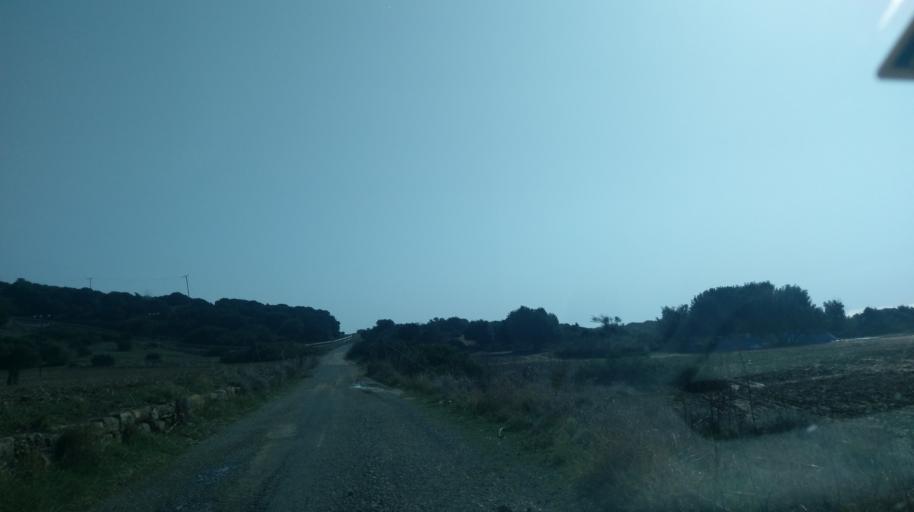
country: CY
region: Ammochostos
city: Rizokarpaso
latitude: 35.6473
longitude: 34.5529
